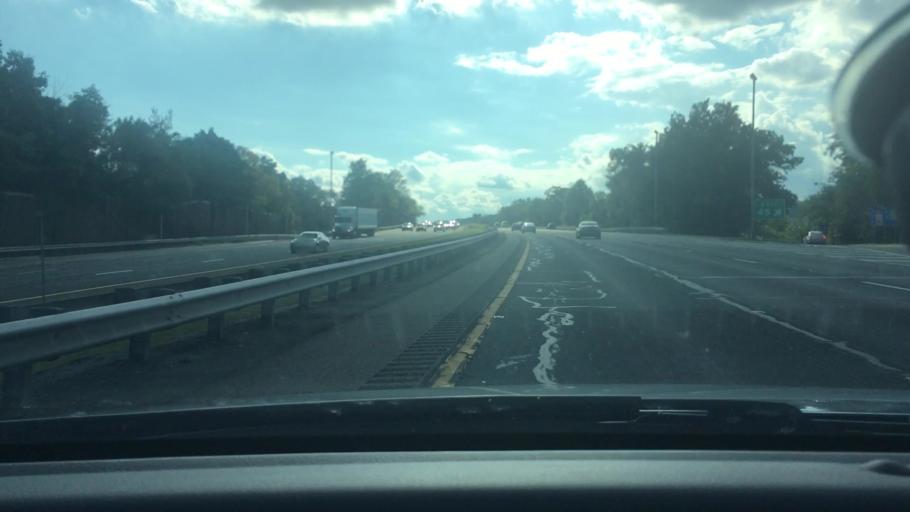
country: US
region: New Jersey
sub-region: Morris County
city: Boonton
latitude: 40.9091
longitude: -74.3916
